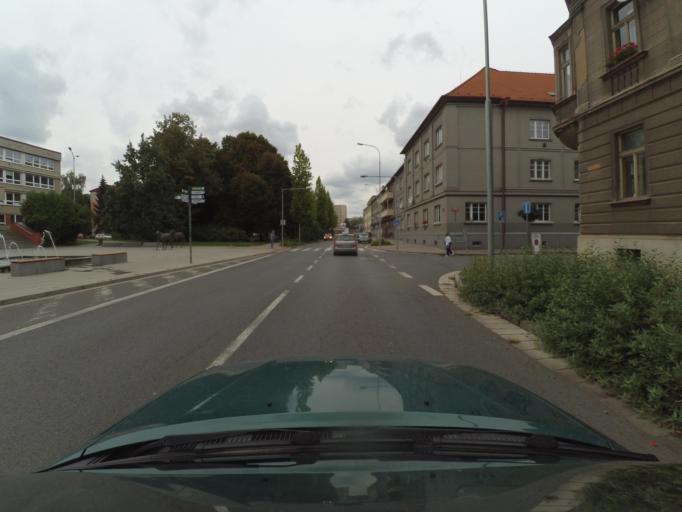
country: CZ
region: Central Bohemia
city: Rakovnik
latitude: 50.1028
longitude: 13.7296
